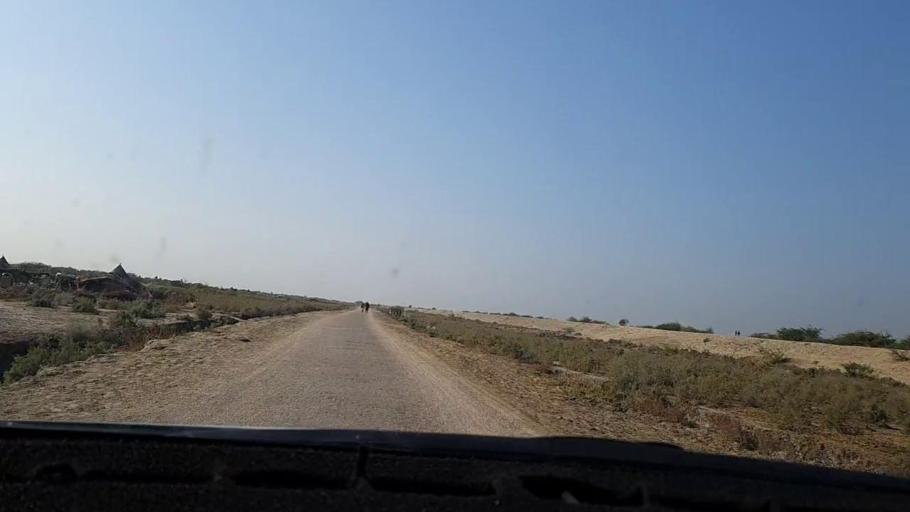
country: PK
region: Sindh
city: Tando Mittha Khan
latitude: 25.8327
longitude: 69.3171
